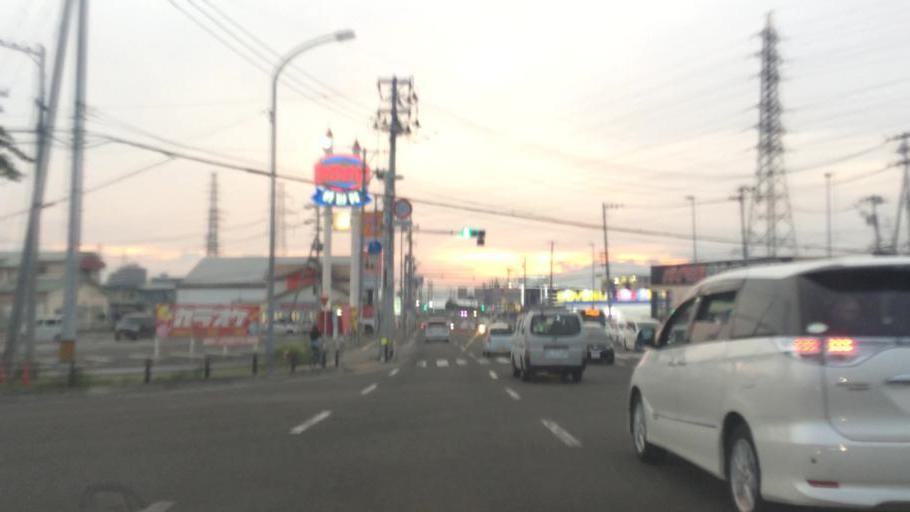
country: JP
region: Miyagi
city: Sendai-shi
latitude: 38.3154
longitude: 140.9008
